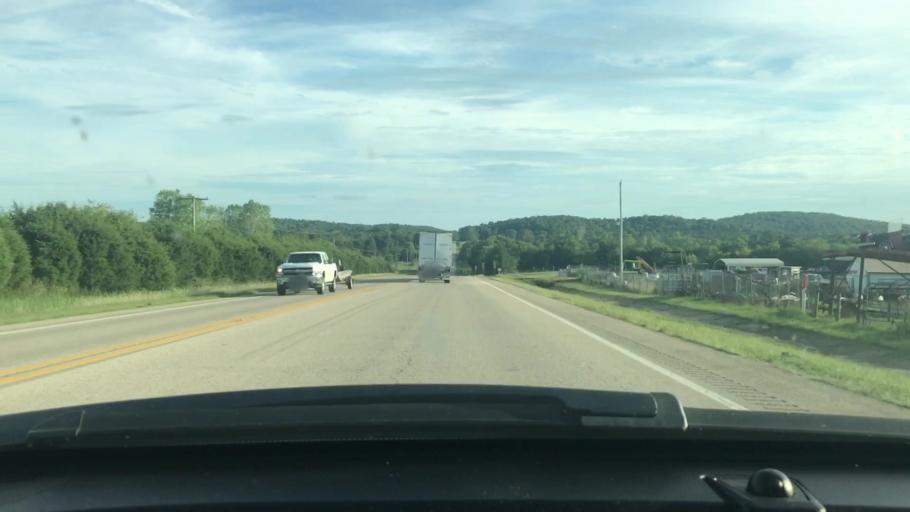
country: US
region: Arkansas
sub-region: Randolph County
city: Pocahontas
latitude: 36.1846
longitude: -91.1626
